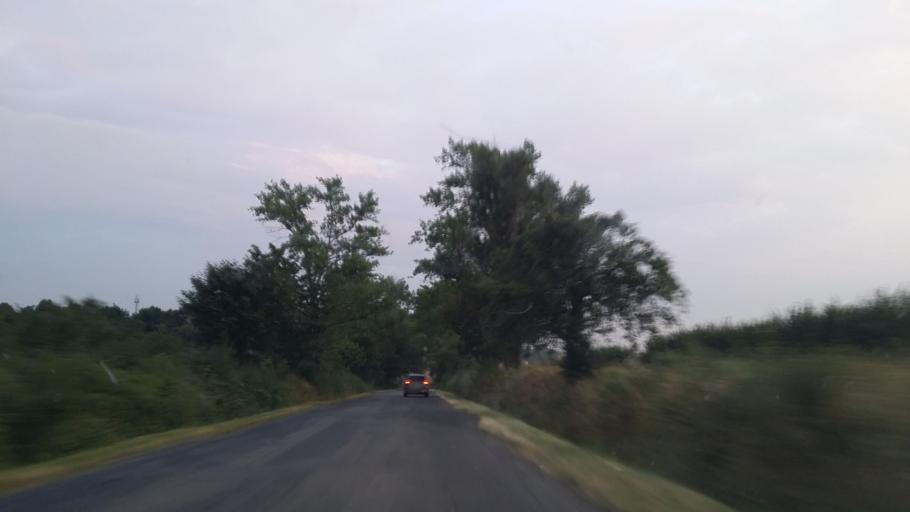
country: PL
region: Lower Silesian Voivodeship
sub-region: Powiat legnicki
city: Legnickie Pole
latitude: 51.1371
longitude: 16.3435
